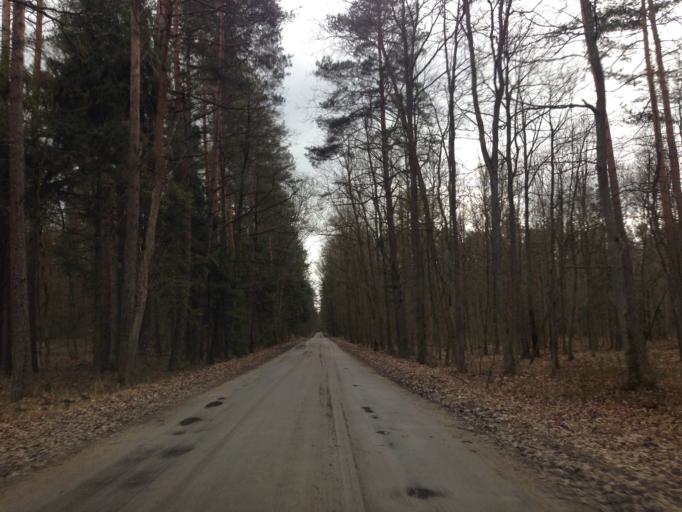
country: PL
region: Kujawsko-Pomorskie
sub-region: Powiat brodnicki
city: Gorzno
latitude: 53.1972
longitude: 19.6947
